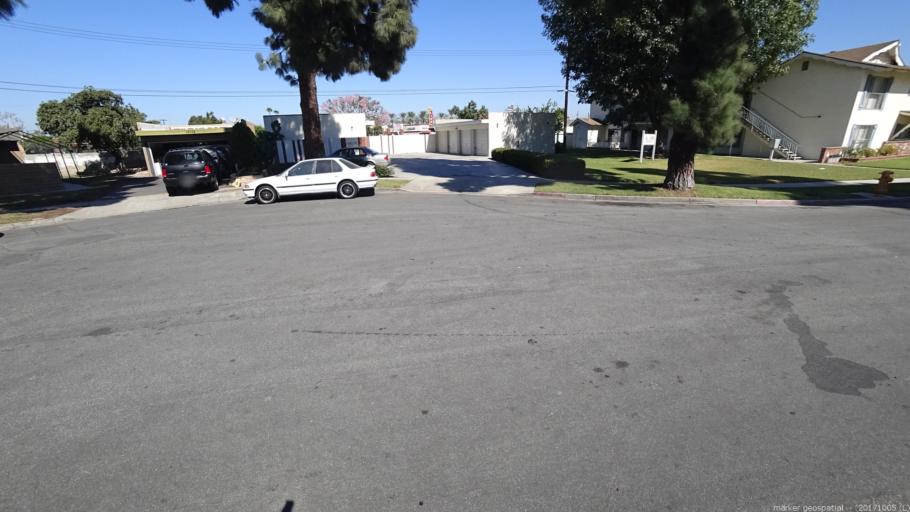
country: US
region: California
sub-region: Orange County
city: Garden Grove
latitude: 33.7879
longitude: -117.9651
